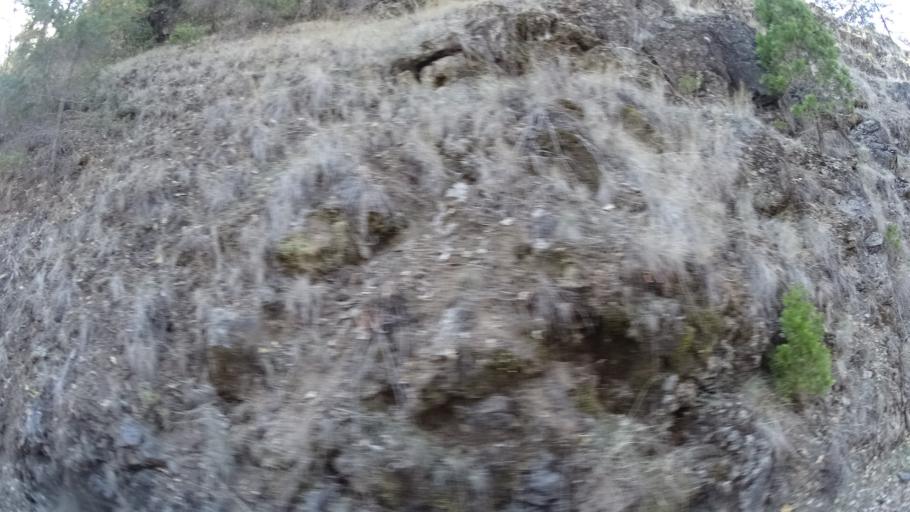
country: US
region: California
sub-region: Siskiyou County
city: Yreka
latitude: 41.8581
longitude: -122.7771
